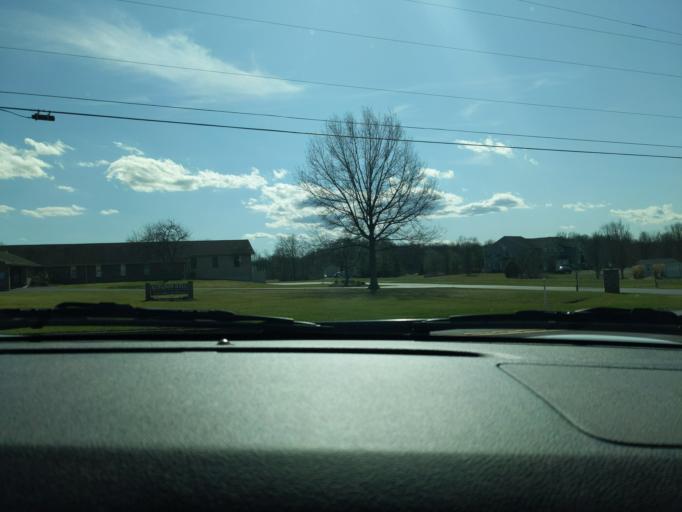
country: US
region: Pennsylvania
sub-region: Bucks County
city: Quakertown
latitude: 40.4385
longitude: -75.3139
